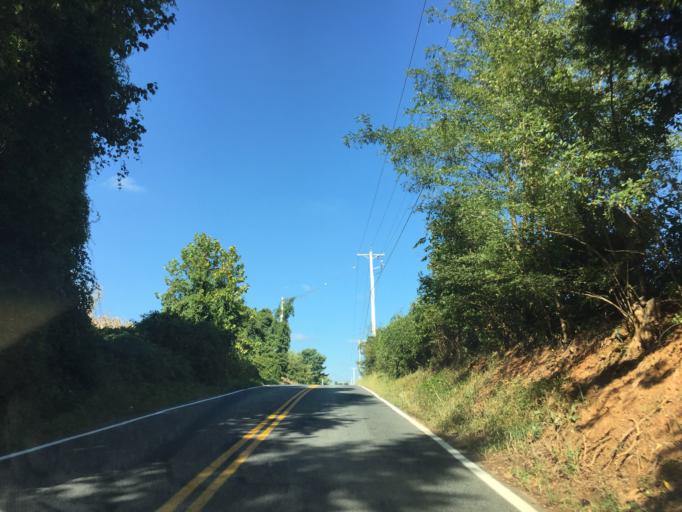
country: US
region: Maryland
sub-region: Harford County
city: Bel Air North
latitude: 39.5760
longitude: -76.4232
